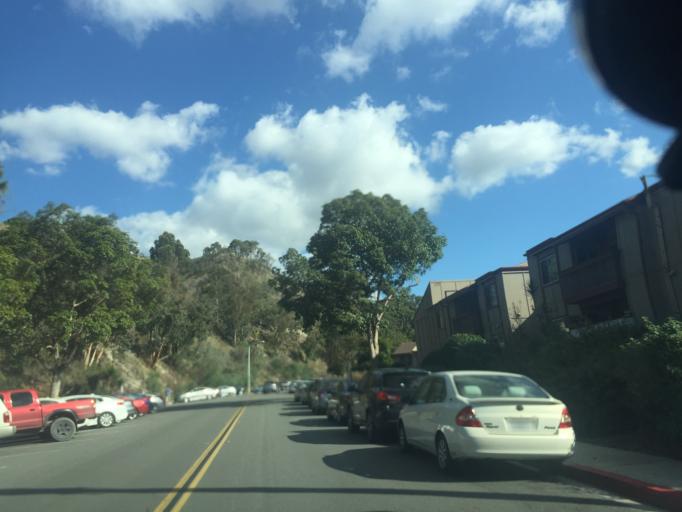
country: US
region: California
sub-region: San Diego County
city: La Mesa
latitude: 32.7816
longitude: -117.0809
